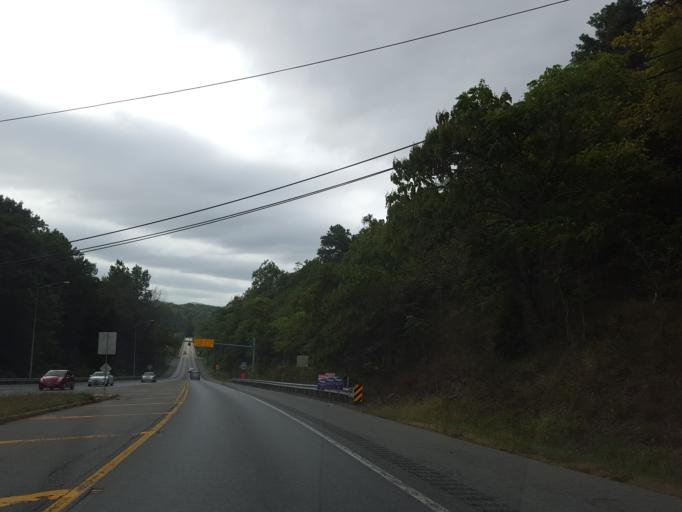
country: US
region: West Virginia
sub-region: Jefferson County
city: Bolivar
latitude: 39.3294
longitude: -77.7039
